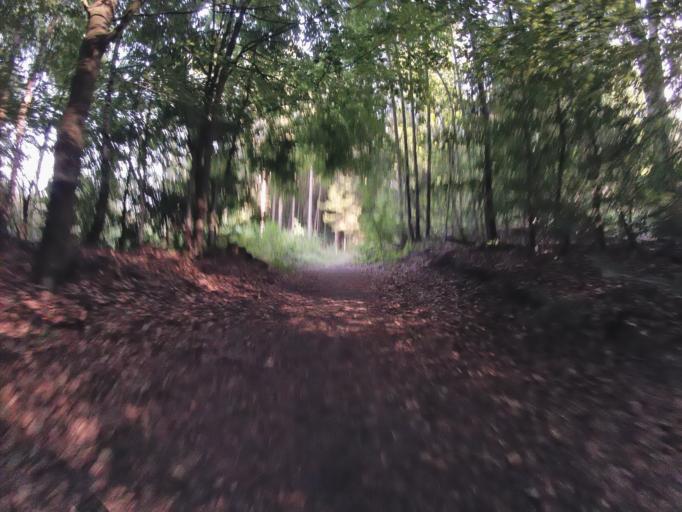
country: DE
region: North Rhine-Westphalia
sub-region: Regierungsbezirk Munster
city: Mettingen
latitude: 52.2841
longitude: 7.8266
